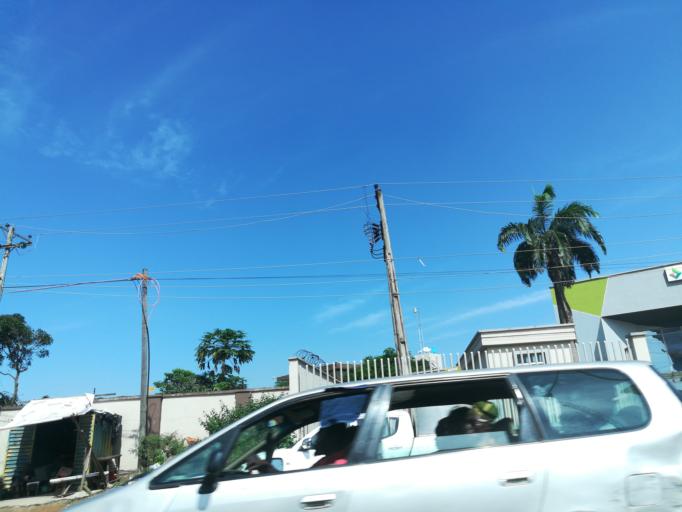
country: NG
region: Lagos
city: Ikeja
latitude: 6.6014
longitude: 3.3439
